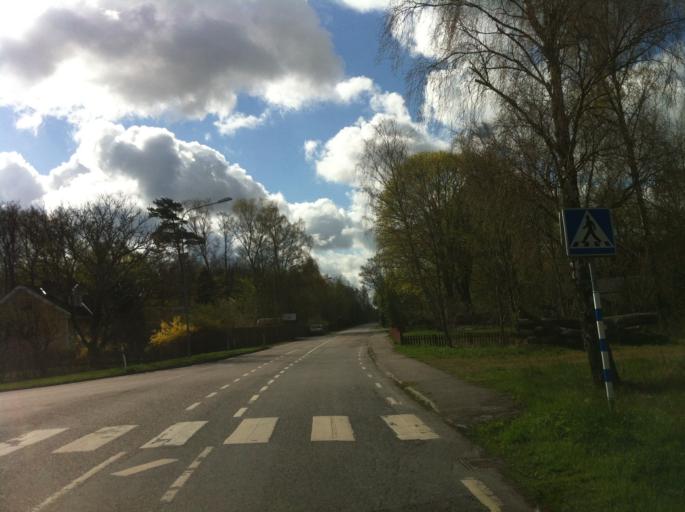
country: SE
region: Skane
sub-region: Hoors Kommun
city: Satofta
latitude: 55.9012
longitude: 13.6084
